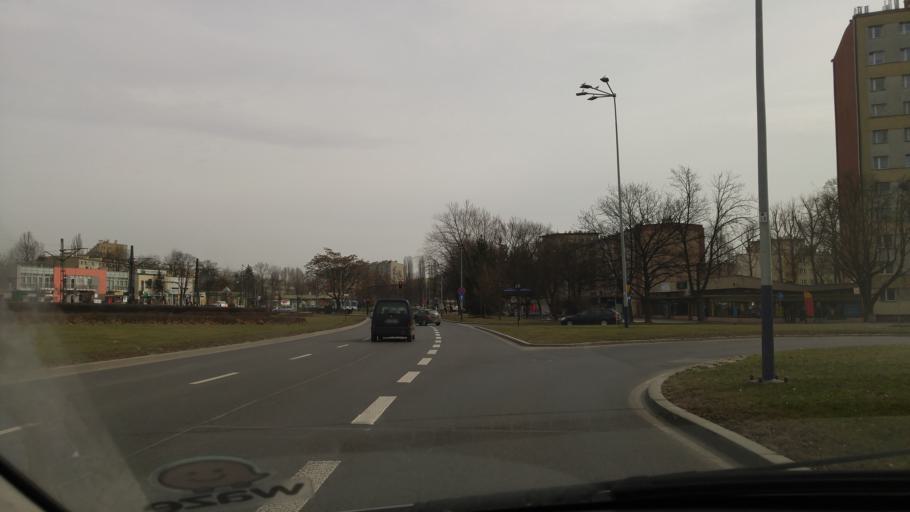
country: PL
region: Lesser Poland Voivodeship
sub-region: Powiat krakowski
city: Michalowice
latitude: 50.0848
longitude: 20.0184
